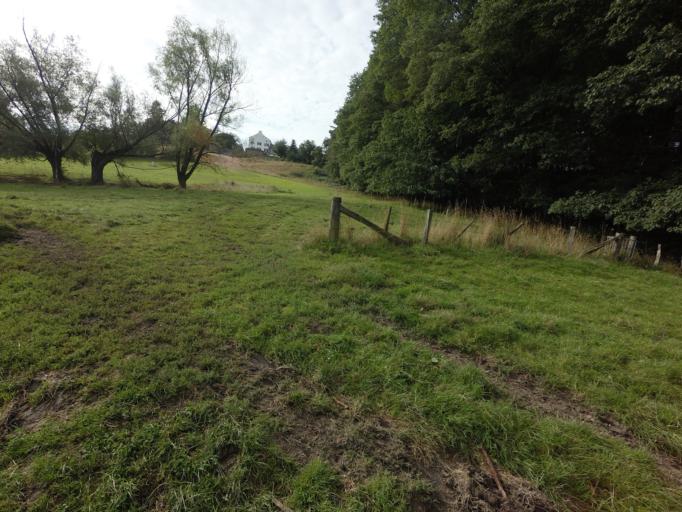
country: BE
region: Wallonia
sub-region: Province de Liege
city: Plombieres
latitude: 50.7402
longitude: 5.9558
